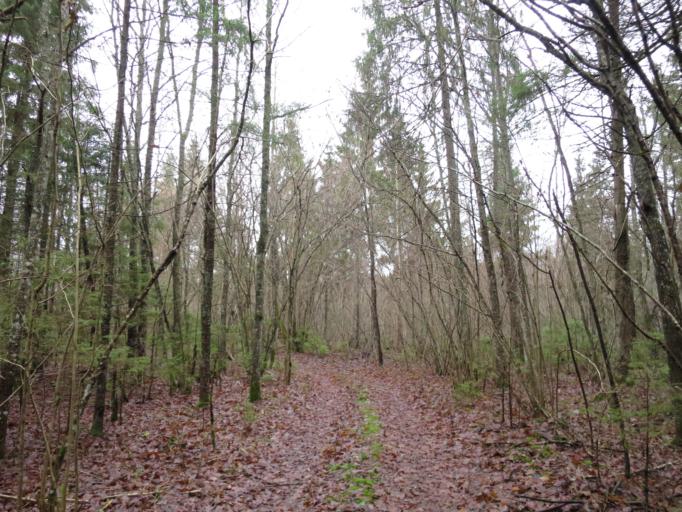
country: LV
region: Malpils
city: Malpils
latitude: 56.9220
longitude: 24.9770
